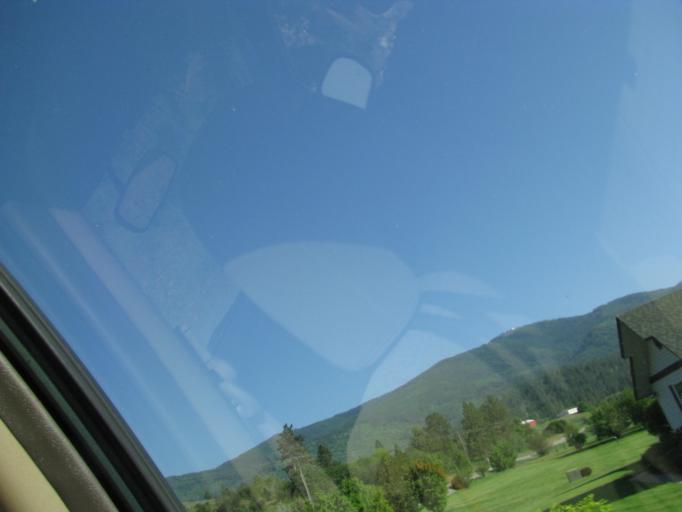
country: US
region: Washington
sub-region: Spokane County
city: Liberty Lake
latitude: 47.6216
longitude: -117.1129
